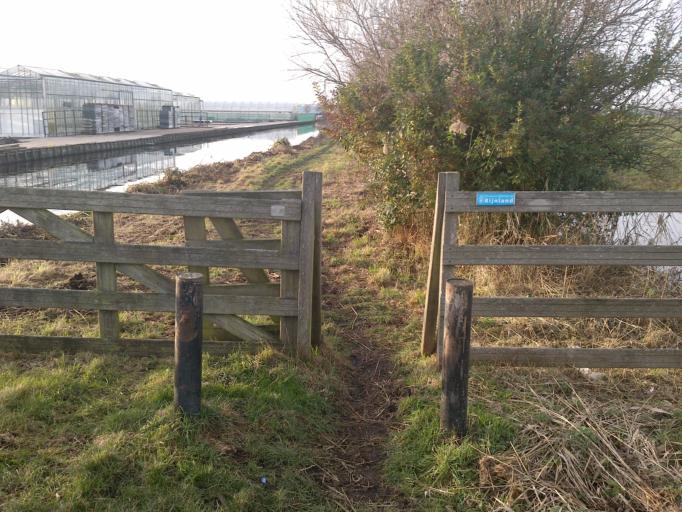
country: NL
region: South Holland
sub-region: Gemeente Boskoop
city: Boskoop
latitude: 52.0969
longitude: 4.6850
